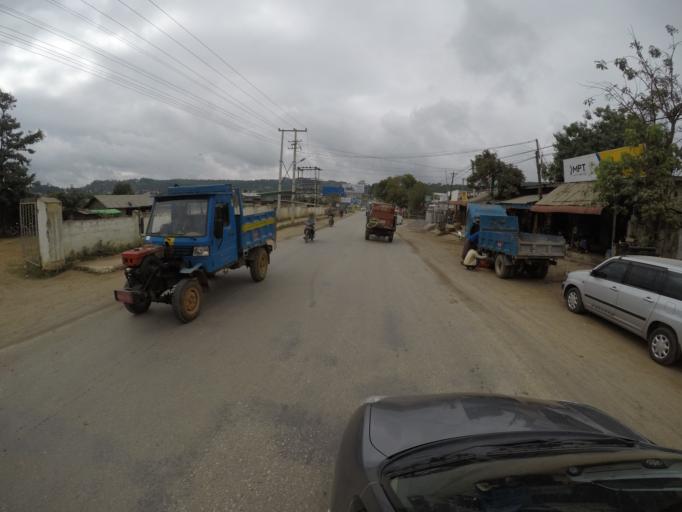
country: MM
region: Shan
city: Taunggyi
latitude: 20.6567
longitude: 96.6309
